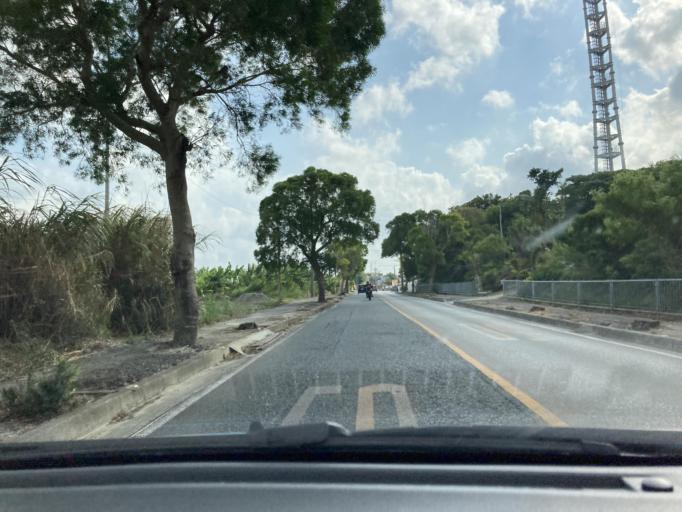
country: JP
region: Okinawa
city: Tomigusuku
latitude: 26.1618
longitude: 127.7315
